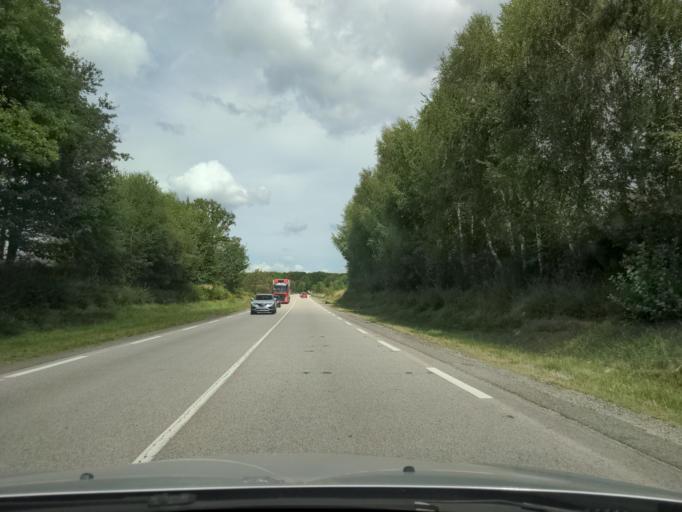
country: FR
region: Limousin
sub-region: Departement de la Haute-Vienne
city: Nieul
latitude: 45.8711
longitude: 1.1645
